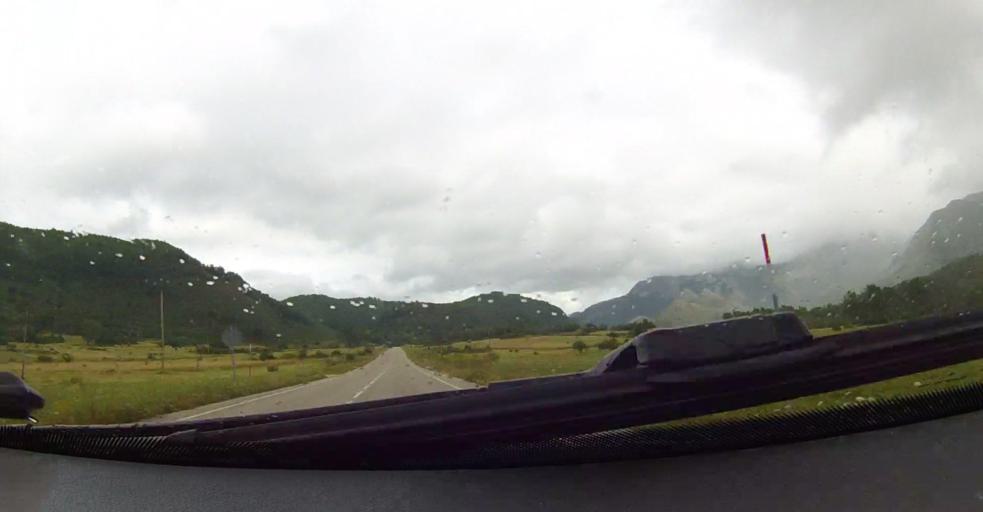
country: ES
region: Castille and Leon
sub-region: Provincia de Leon
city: Acebedo
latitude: 43.0394
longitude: -5.0884
